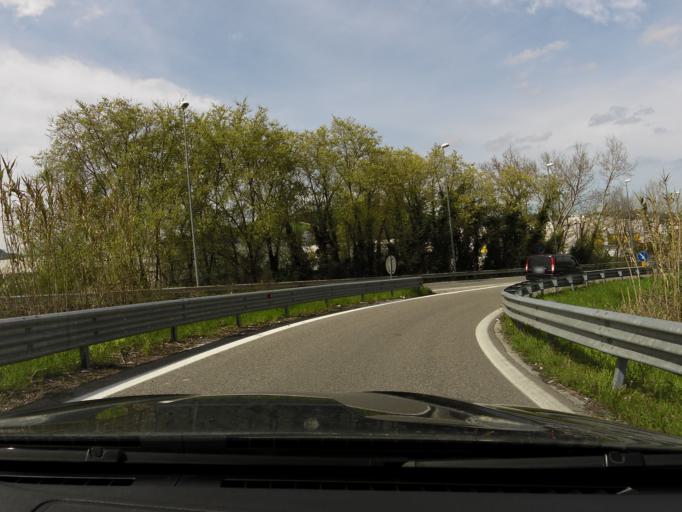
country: IT
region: The Marches
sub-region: Provincia di Ancona
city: San Biagio
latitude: 43.5333
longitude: 13.5132
